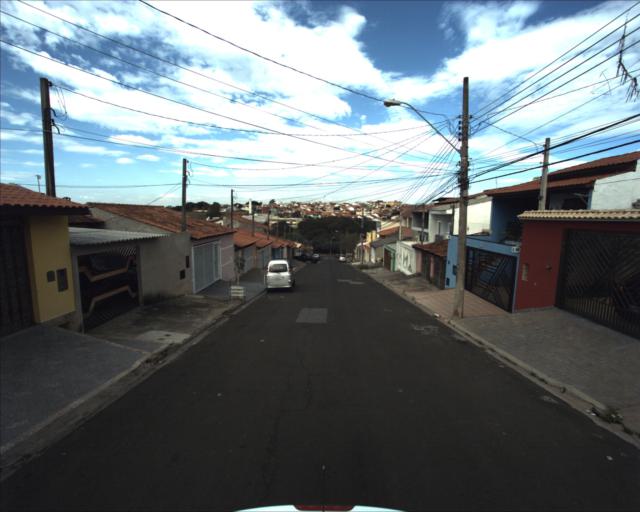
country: BR
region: Sao Paulo
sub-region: Sorocaba
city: Sorocaba
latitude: -23.4879
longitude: -47.5099
